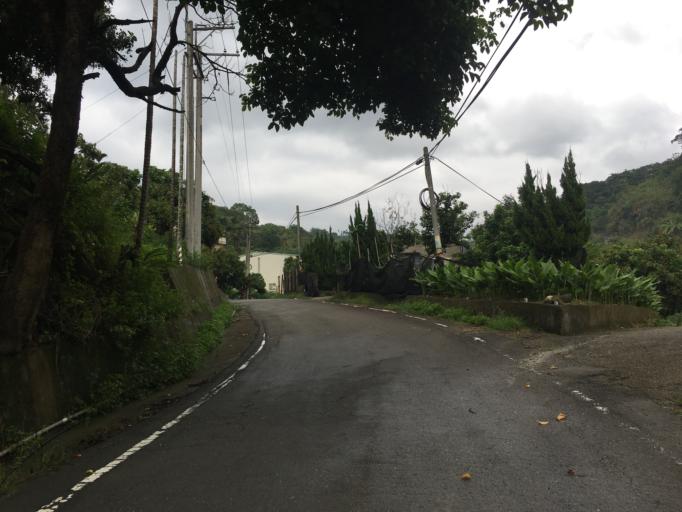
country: TW
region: Taiwan
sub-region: Taichung City
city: Taichung
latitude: 24.0601
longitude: 120.7464
